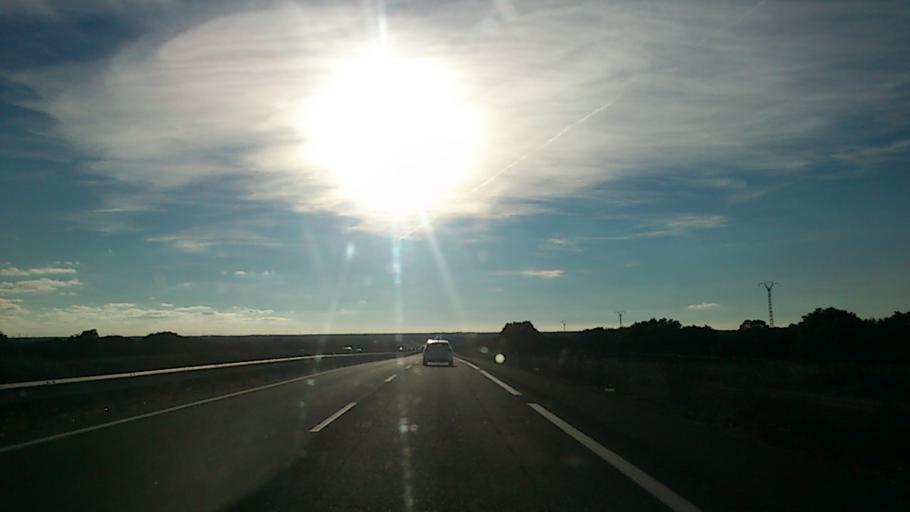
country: ES
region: Castille-La Mancha
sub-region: Provincia de Guadalajara
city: Mirabueno
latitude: 40.9410
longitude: -2.6992
